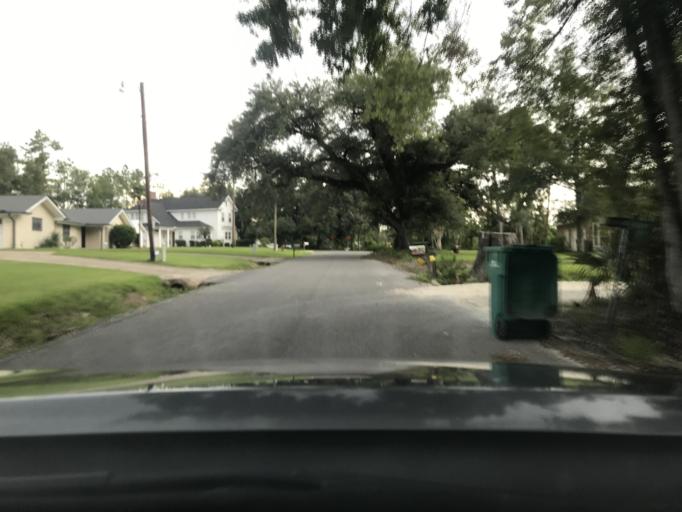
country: US
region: Louisiana
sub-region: Calcasieu Parish
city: Westlake
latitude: 30.2835
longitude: -93.2326
